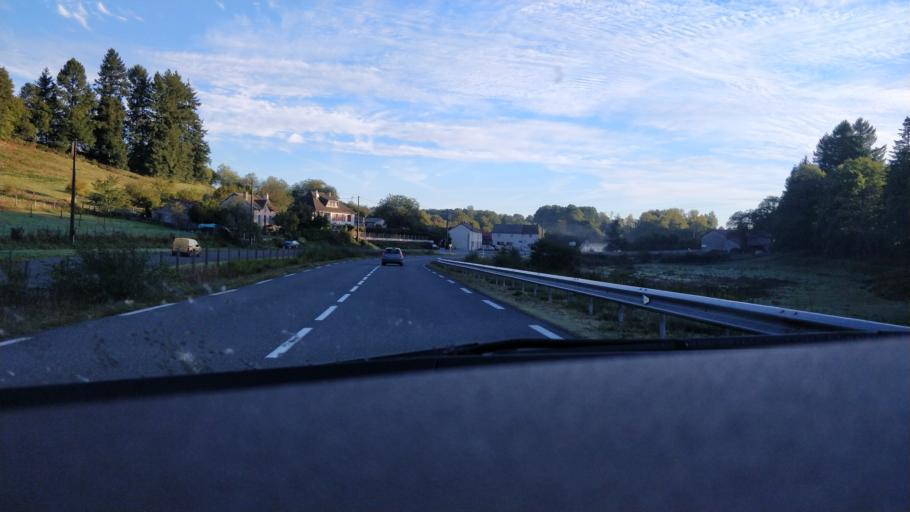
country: FR
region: Limousin
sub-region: Departement de la Creuse
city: Bourganeuf
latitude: 45.9480
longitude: 1.6836
